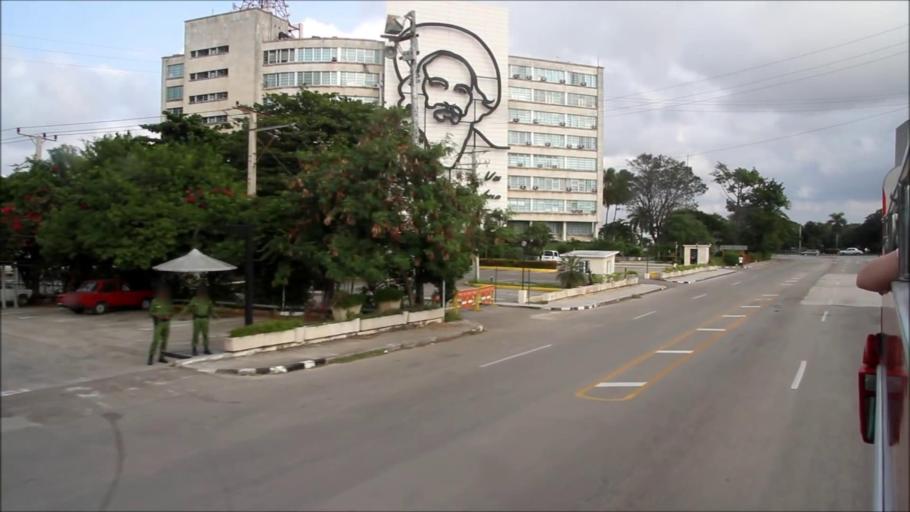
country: CU
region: La Habana
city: Havana
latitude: 23.1252
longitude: -82.3856
